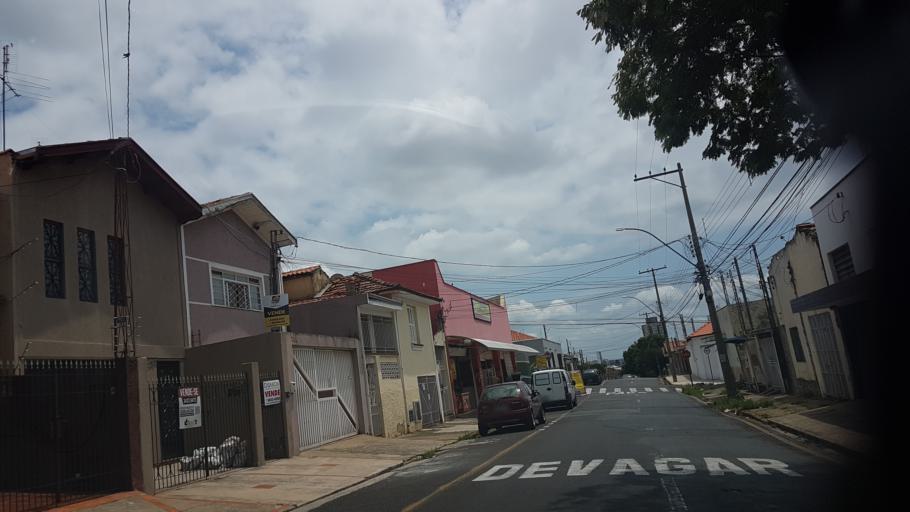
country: BR
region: Sao Paulo
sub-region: Piracicaba
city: Piracicaba
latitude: -22.7425
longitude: -47.6542
